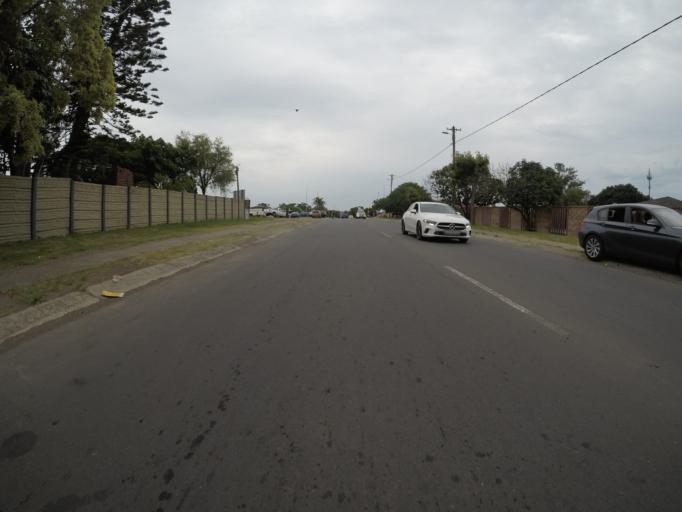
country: ZA
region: Eastern Cape
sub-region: Buffalo City Metropolitan Municipality
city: East London
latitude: -32.9919
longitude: 27.8624
